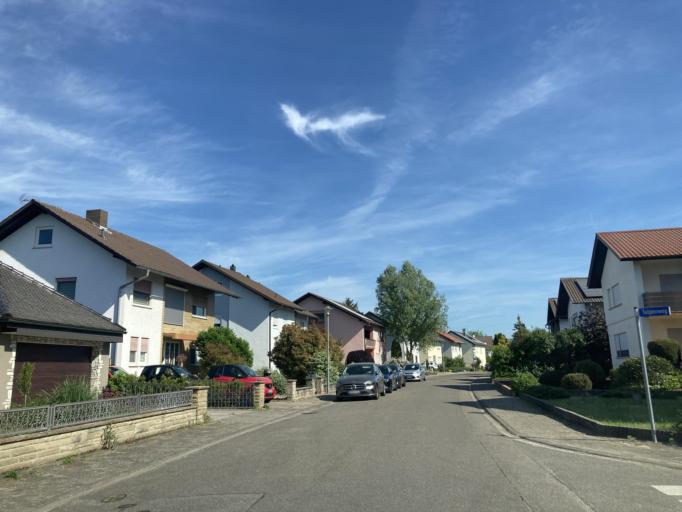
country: DE
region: Baden-Wuerttemberg
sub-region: Karlsruhe Region
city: Kronau
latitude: 49.2033
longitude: 8.6348
